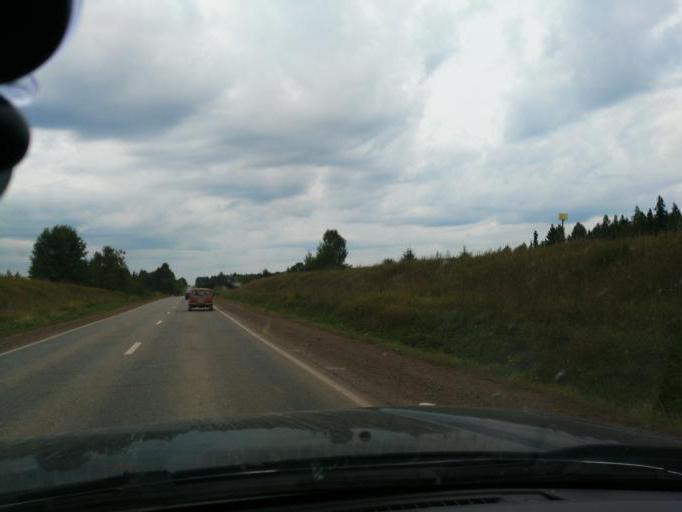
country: RU
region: Perm
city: Chernushka
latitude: 56.7467
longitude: 56.1577
